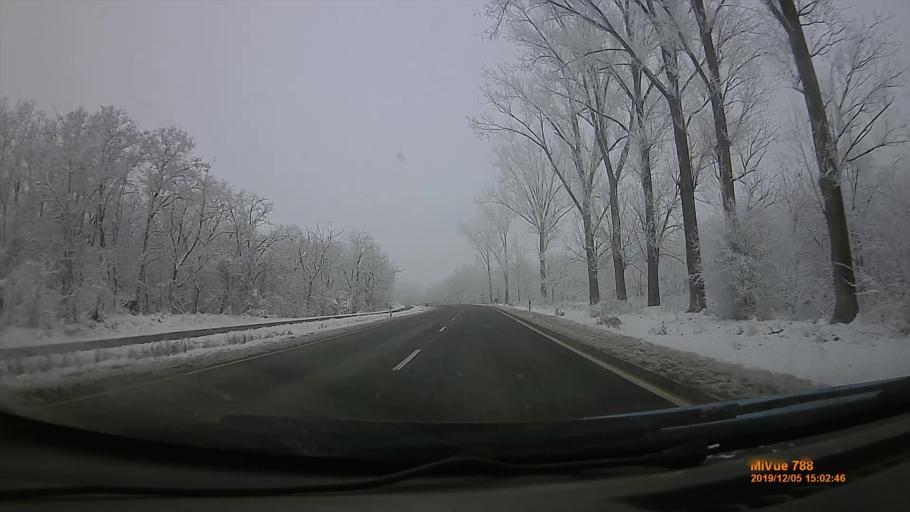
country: HU
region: Szabolcs-Szatmar-Bereg
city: Tiszanagyfalu
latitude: 48.0791
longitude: 21.5091
